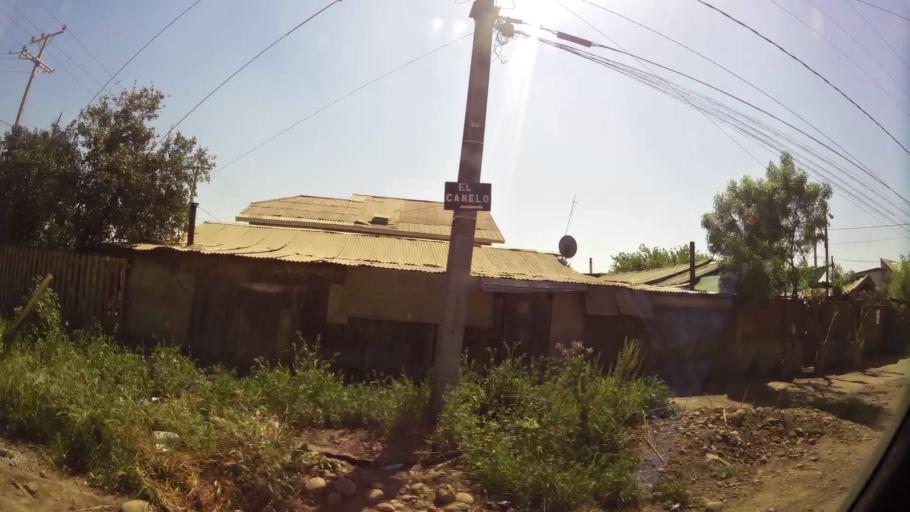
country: CL
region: Santiago Metropolitan
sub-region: Provincia de Talagante
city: Penaflor
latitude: -33.5805
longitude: -70.8056
